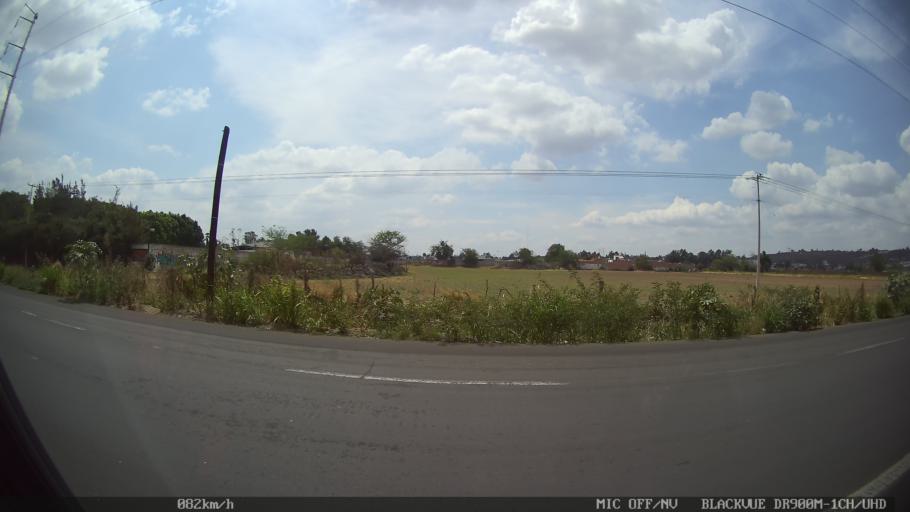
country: MX
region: Jalisco
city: Tonala
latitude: 20.6499
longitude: -103.2356
